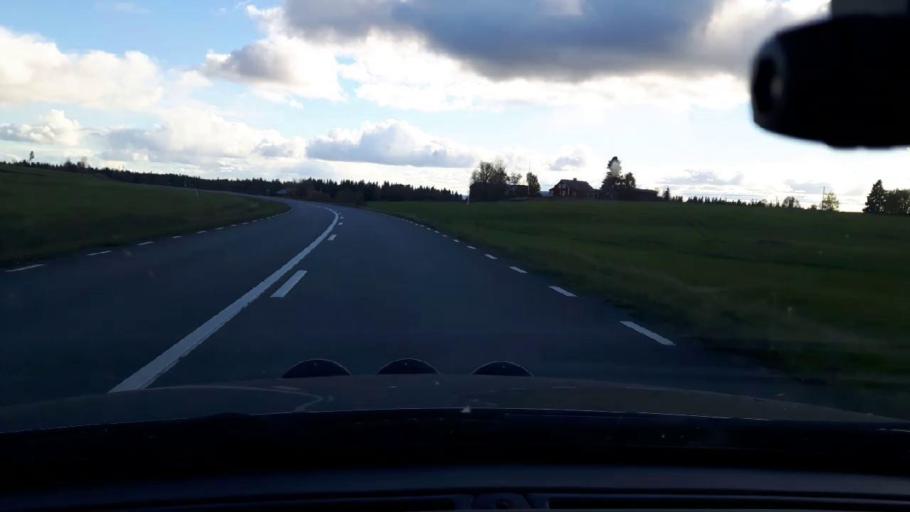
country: SE
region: Jaemtland
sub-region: Krokoms Kommun
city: Krokom
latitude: 63.0794
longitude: 14.2913
